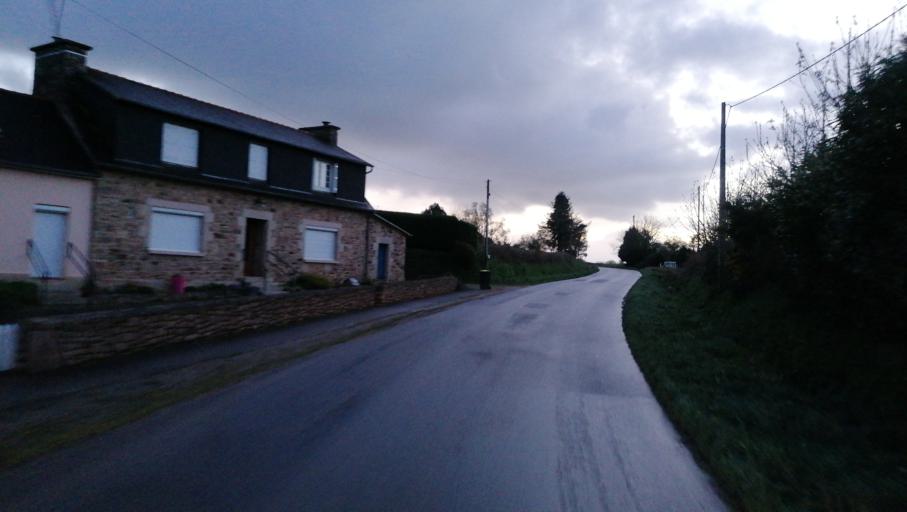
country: FR
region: Brittany
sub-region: Departement des Cotes-d'Armor
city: Lanvollon
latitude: 48.6706
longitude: -2.9714
